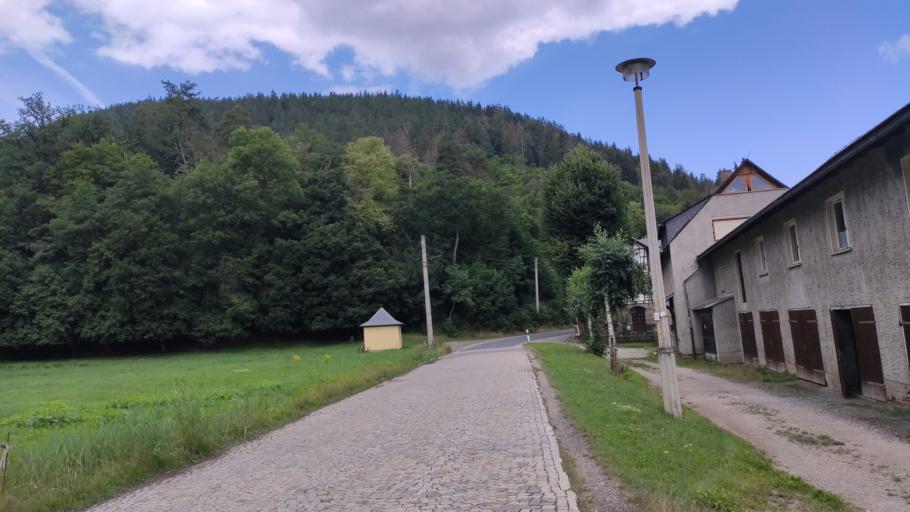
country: DE
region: Thuringia
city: Leutenberg
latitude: 50.5658
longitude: 11.4462
